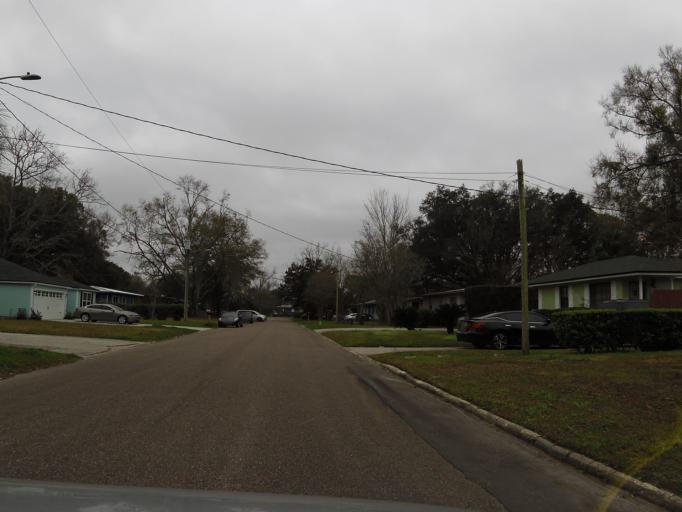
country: US
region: Florida
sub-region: Duval County
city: Jacksonville
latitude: 30.3697
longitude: -81.7171
